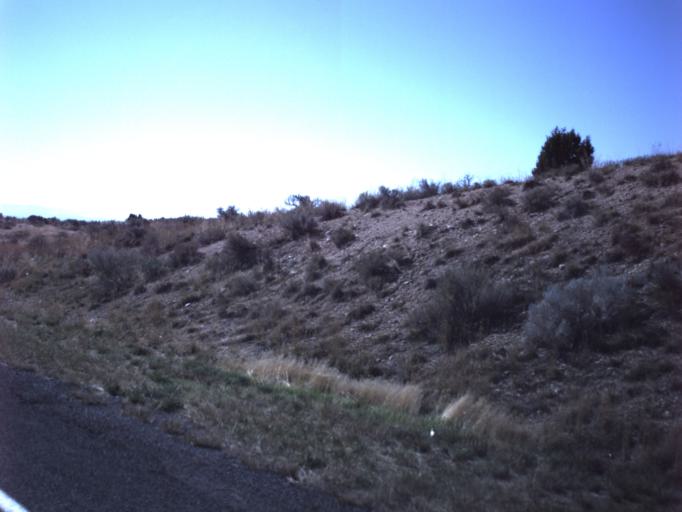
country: US
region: Utah
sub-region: Sanpete County
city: Gunnison
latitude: 39.2800
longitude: -111.8790
